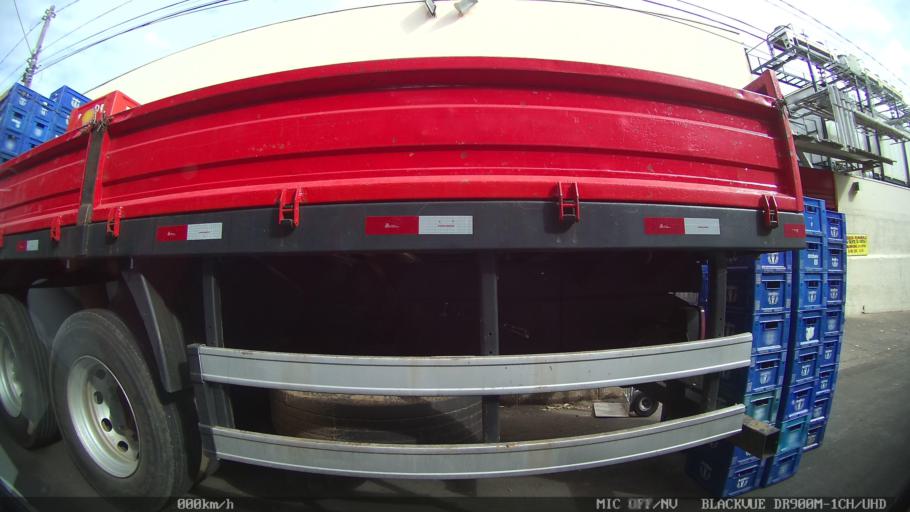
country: BR
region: Sao Paulo
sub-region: Sao Jose Do Rio Preto
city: Sao Jose do Rio Preto
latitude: -20.8245
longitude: -49.3732
